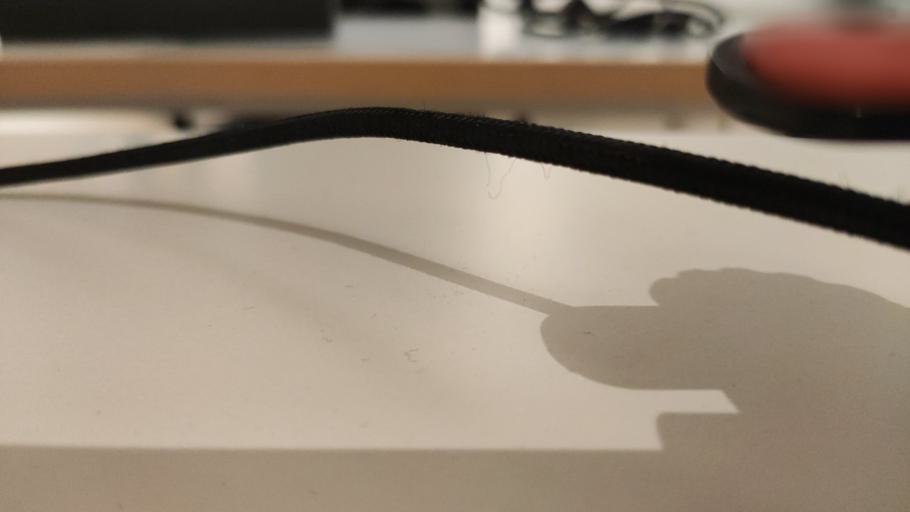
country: RU
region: Moskovskaya
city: Dorokhovo
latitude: 55.4917
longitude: 36.3531
